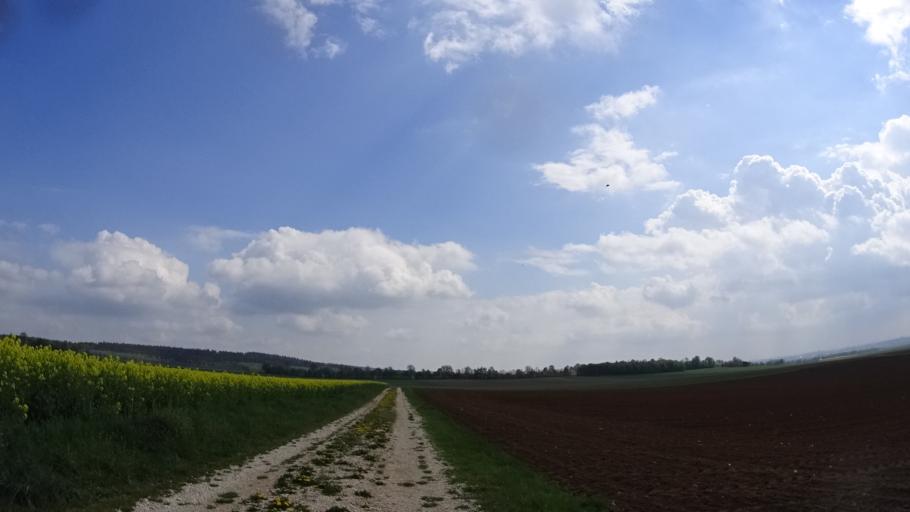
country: DE
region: Bavaria
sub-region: Upper Bavaria
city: Hitzhofen
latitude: 48.8408
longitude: 11.3272
